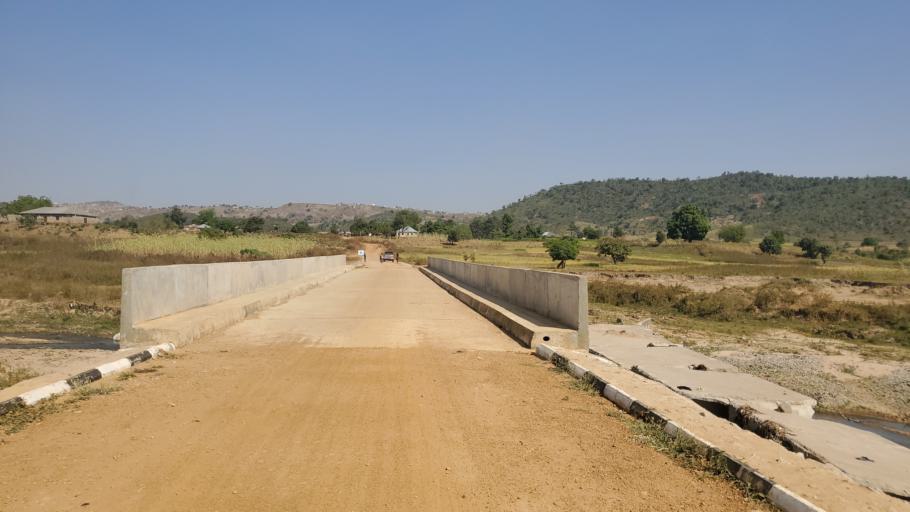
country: NG
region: Niger
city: Suleja
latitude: 9.1841
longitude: 7.1375
